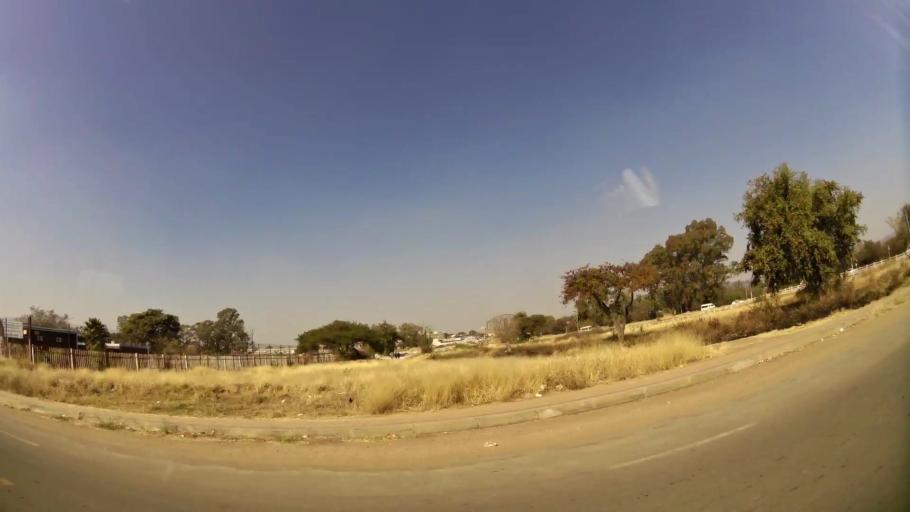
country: ZA
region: North-West
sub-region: Bojanala Platinum District Municipality
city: Rustenburg
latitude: -25.6606
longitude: 27.2312
